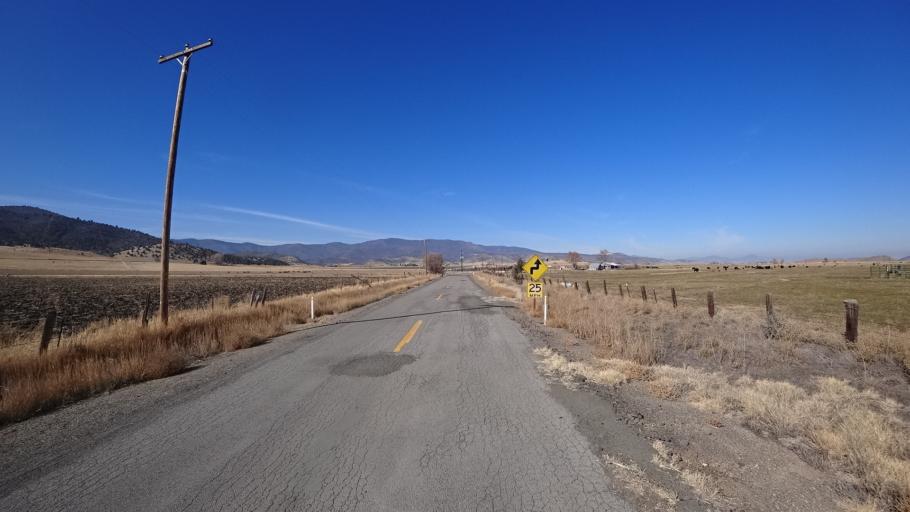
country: US
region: California
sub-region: Siskiyou County
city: Weed
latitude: 41.5248
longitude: -122.5298
